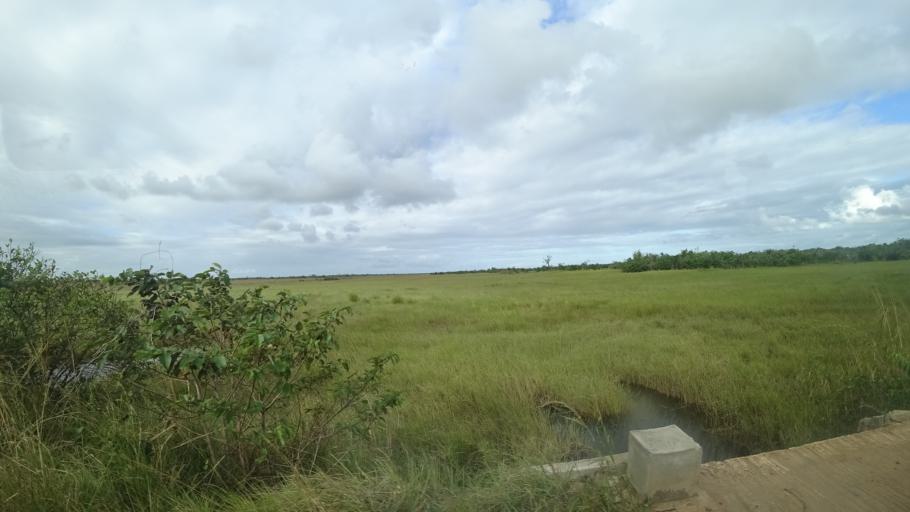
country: MZ
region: Sofala
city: Beira
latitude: -19.6283
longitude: 35.0603
